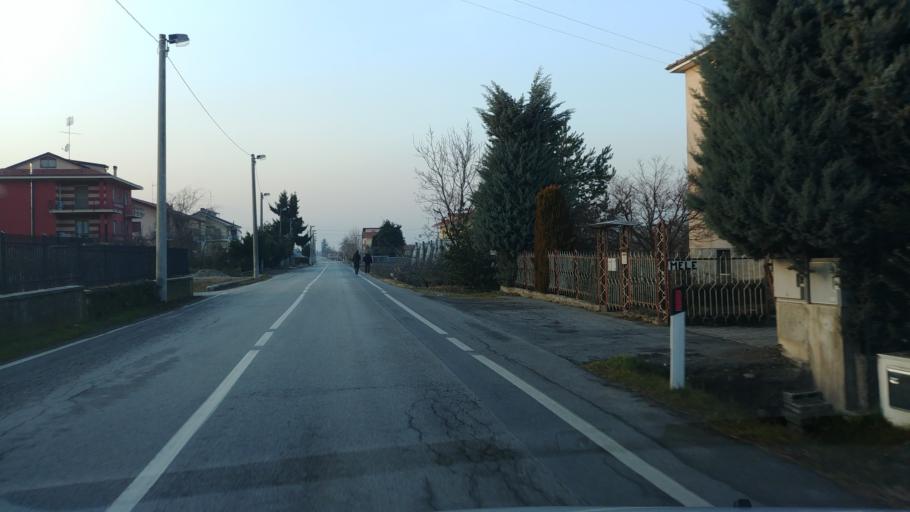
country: IT
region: Piedmont
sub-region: Provincia di Cuneo
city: Cuneo
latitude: 44.4155
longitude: 7.5396
